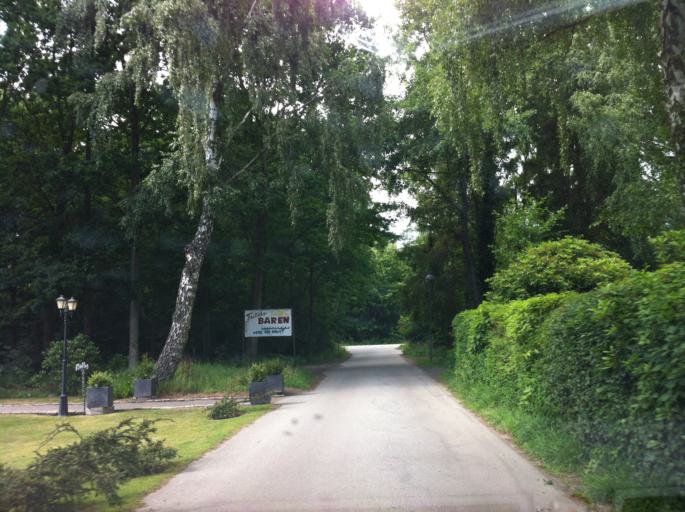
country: SE
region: Skane
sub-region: Ystads Kommun
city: Ystad
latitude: 55.4305
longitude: 13.8610
